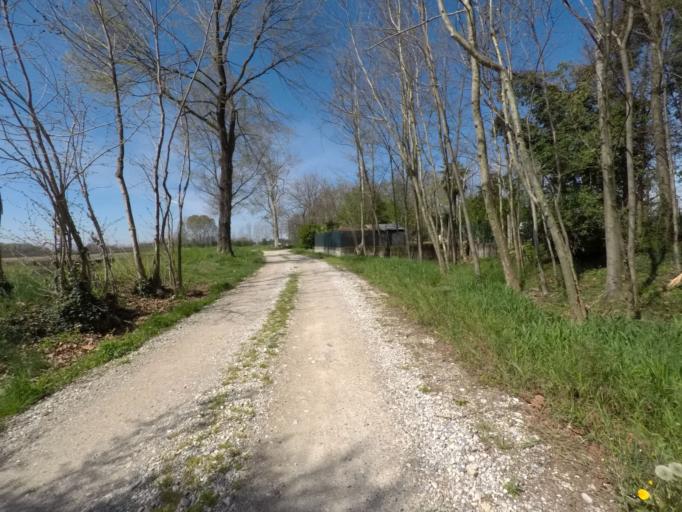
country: IT
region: Friuli Venezia Giulia
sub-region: Provincia di Udine
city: Codroipo
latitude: 45.9559
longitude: 12.9711
